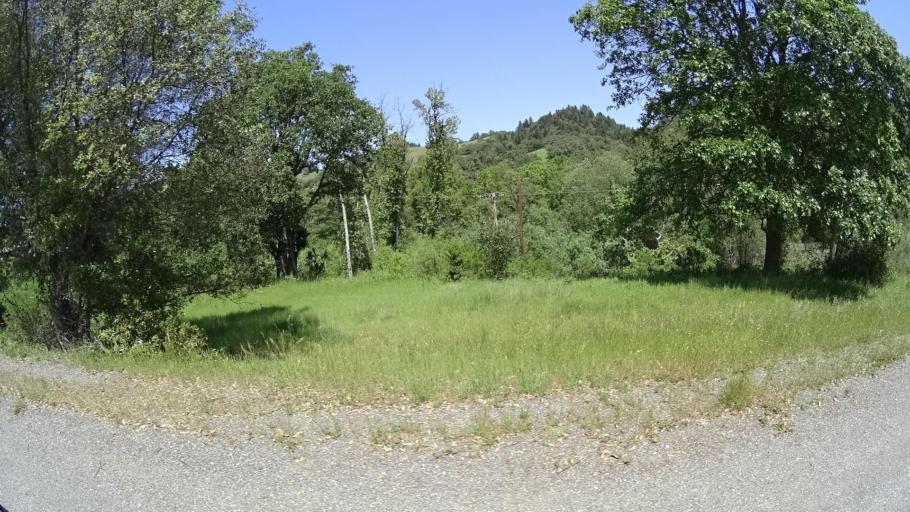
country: US
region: California
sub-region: Humboldt County
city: Redway
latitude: 40.2168
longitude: -123.6359
